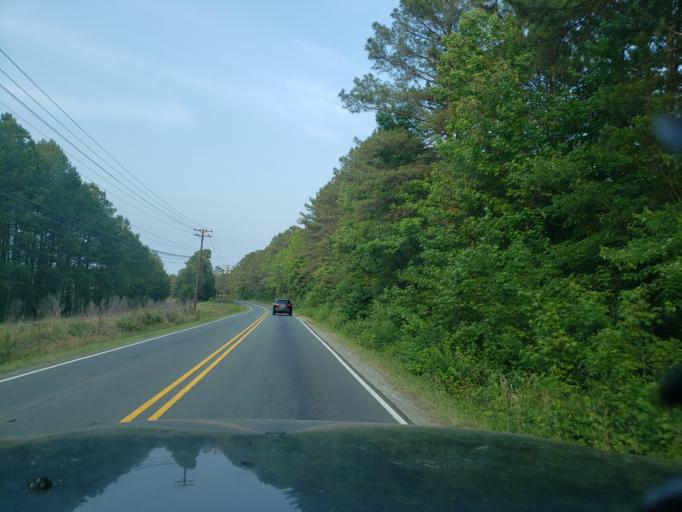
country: US
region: North Carolina
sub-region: Durham County
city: Durham
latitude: 35.9568
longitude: -78.8816
